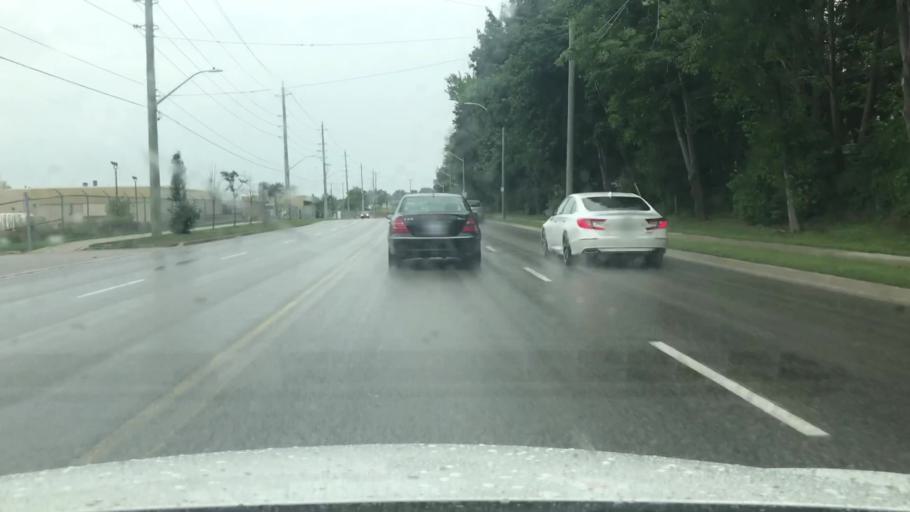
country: CA
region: Ontario
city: Bradford West Gwillimbury
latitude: 44.1252
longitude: -79.5572
